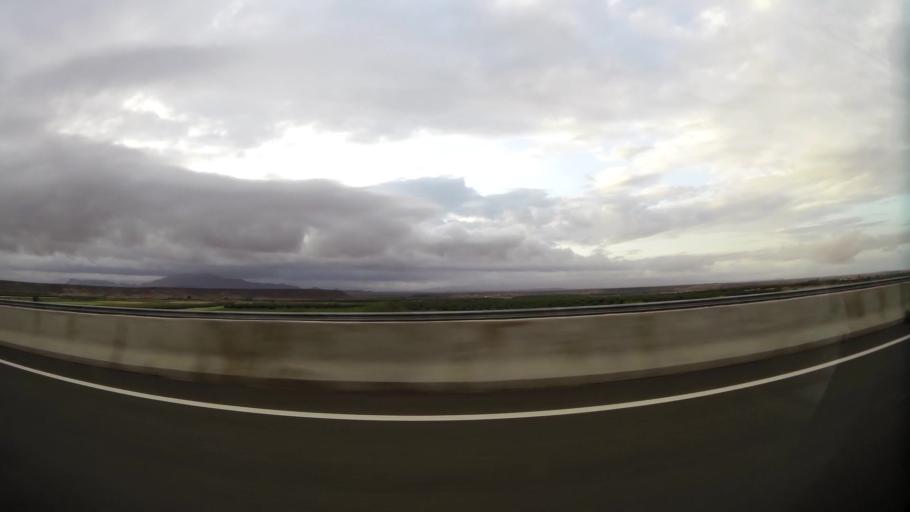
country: MA
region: Taza-Al Hoceima-Taounate
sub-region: Taza
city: Guercif
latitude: 34.4009
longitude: -3.1949
